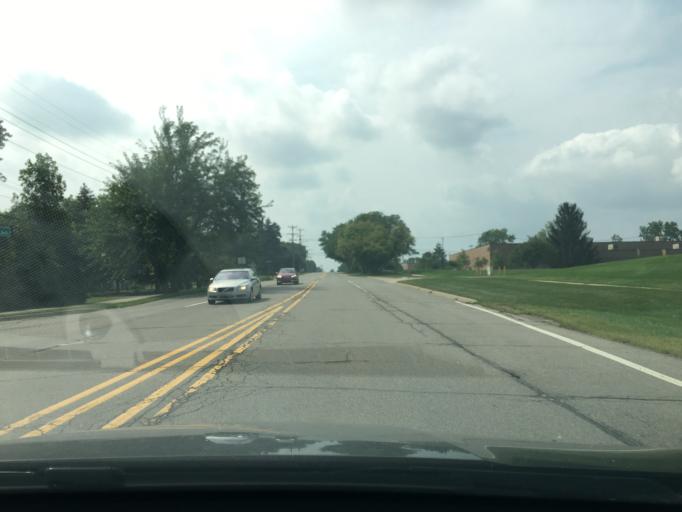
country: US
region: Michigan
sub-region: Oakland County
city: Rochester Hills
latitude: 42.6346
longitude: -83.1871
